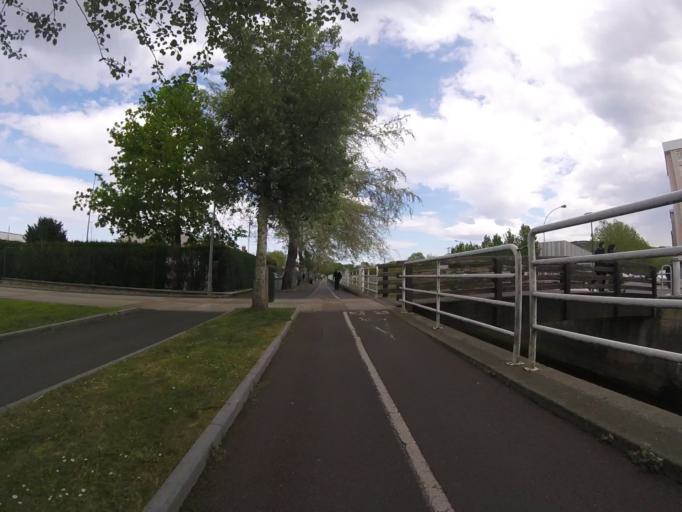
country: ES
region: Basque Country
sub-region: Provincia de Guipuzcoa
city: Zarautz
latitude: 43.2813
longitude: -2.1613
